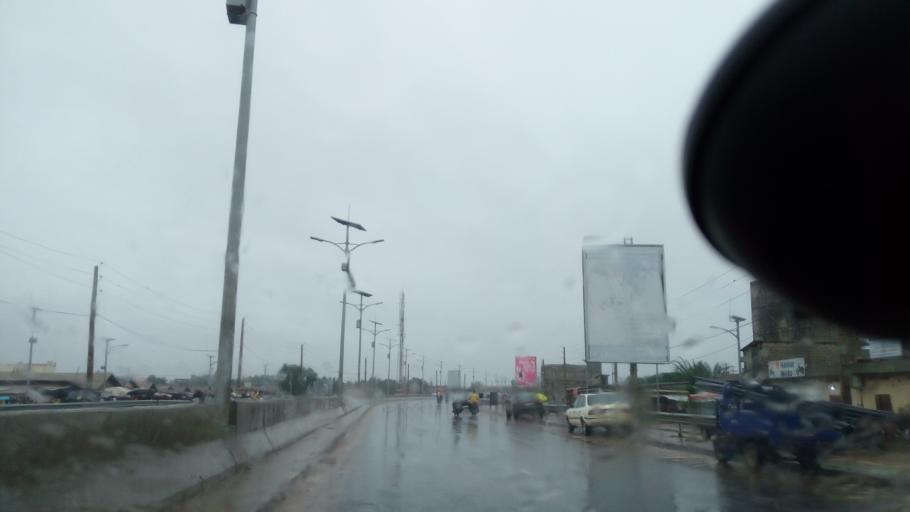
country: BJ
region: Atlantique
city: Hevie
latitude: 6.3877
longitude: 2.2774
